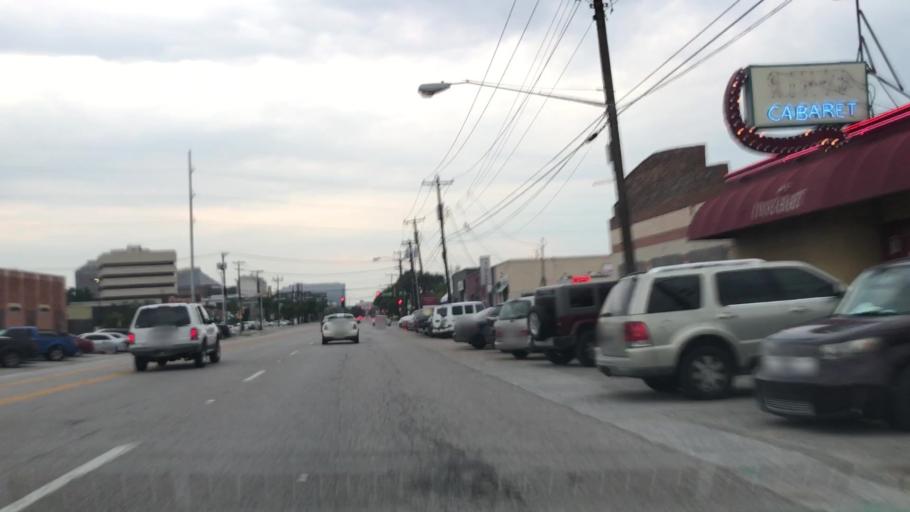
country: US
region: Texas
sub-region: Dallas County
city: Dallas
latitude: 32.7921
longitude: -96.8216
